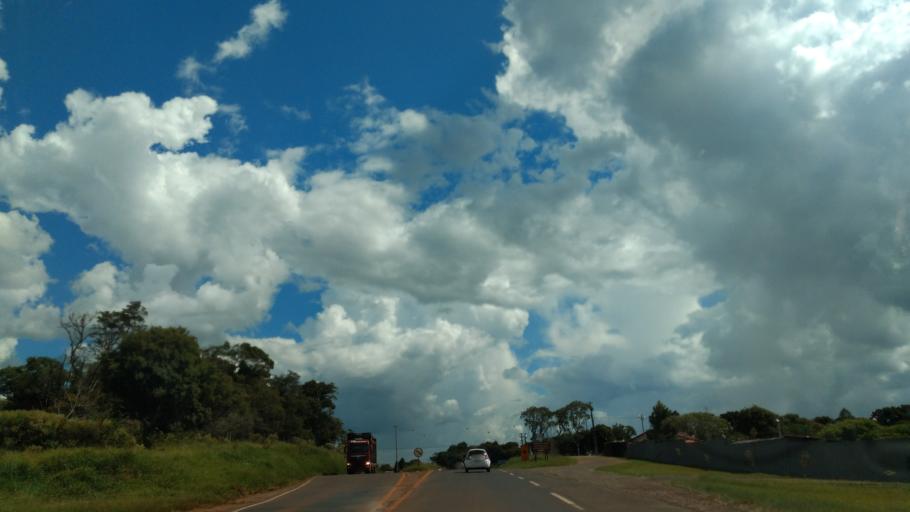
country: BR
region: Parana
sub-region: Guarapuava
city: Guarapuava
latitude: -25.4268
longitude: -51.4920
